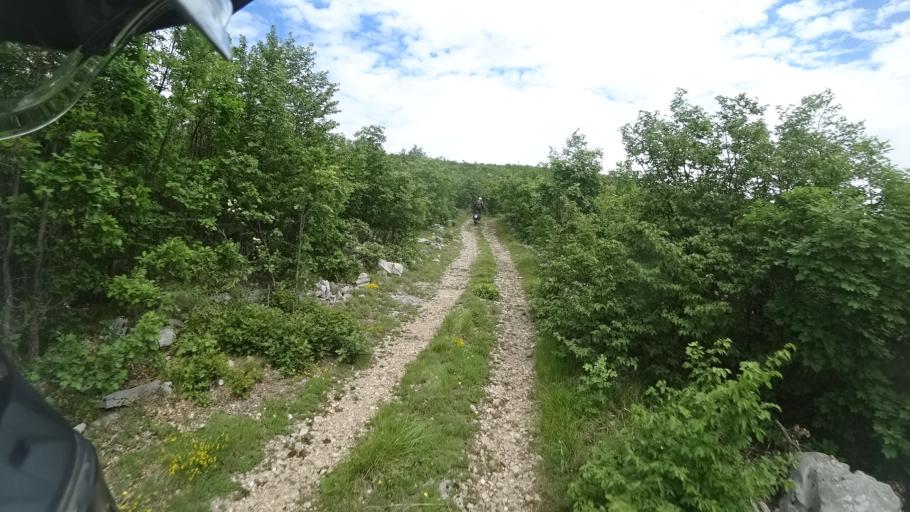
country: HR
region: Splitsko-Dalmatinska
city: Hrvace
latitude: 43.8840
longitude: 16.5881
